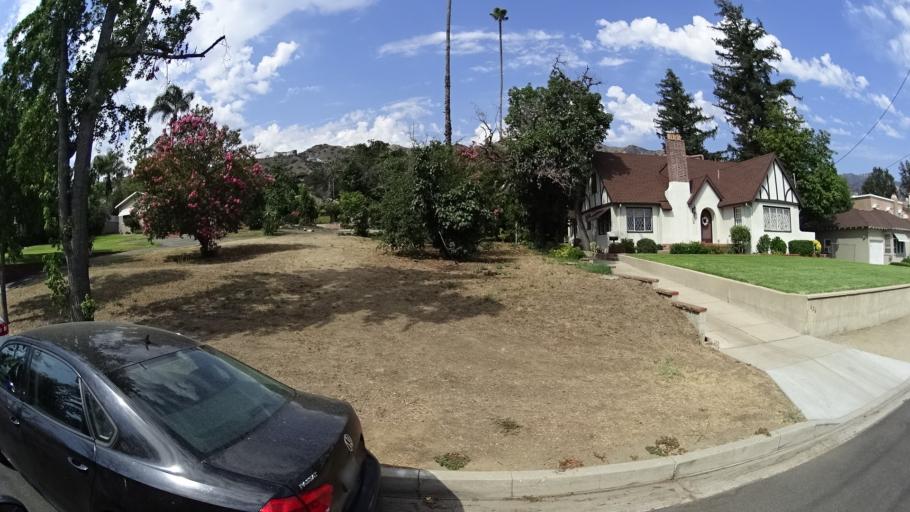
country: US
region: California
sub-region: Los Angeles County
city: Burbank
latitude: 34.1885
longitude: -118.2907
